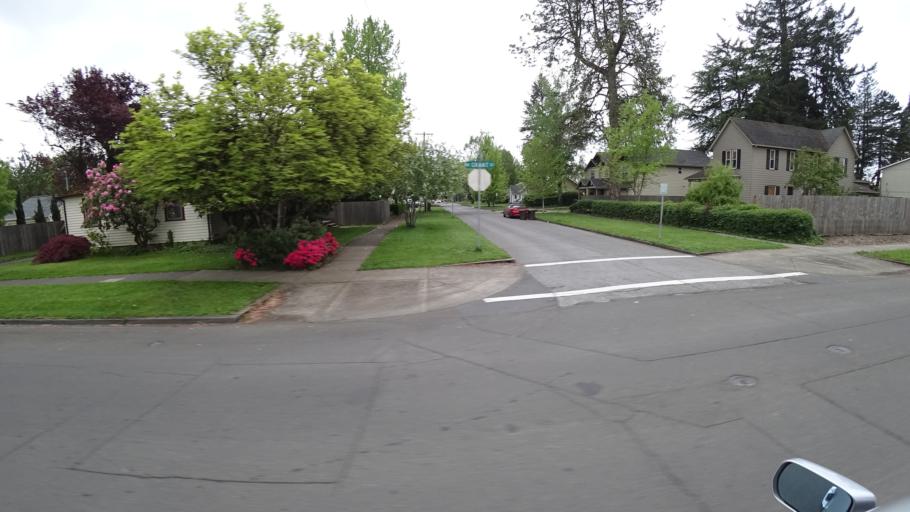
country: US
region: Oregon
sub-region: Washington County
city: Hillsboro
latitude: 45.5284
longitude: -122.9876
